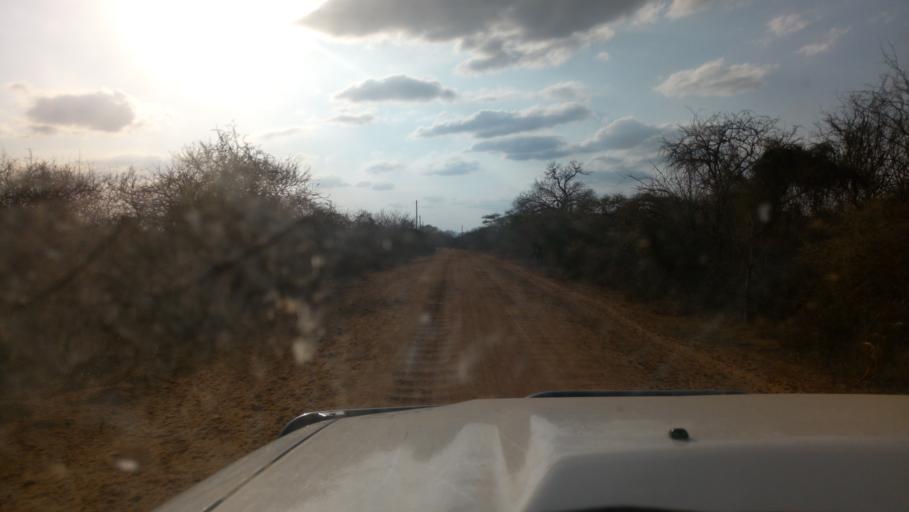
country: KE
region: Kitui
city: Kitui
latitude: -1.6905
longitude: 38.3527
